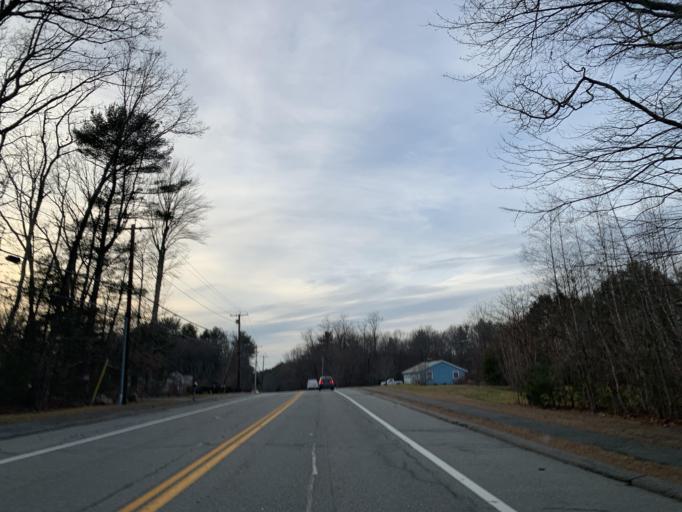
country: US
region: Rhode Island
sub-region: Providence County
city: Chepachet
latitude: 41.9190
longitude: -71.6875
